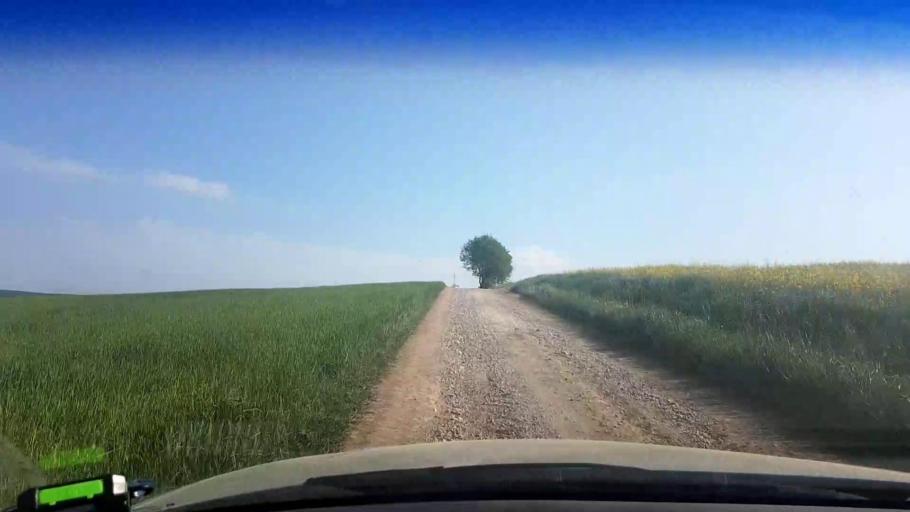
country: DE
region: Bavaria
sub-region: Upper Franconia
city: Memmelsdorf
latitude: 49.9685
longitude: 10.9843
